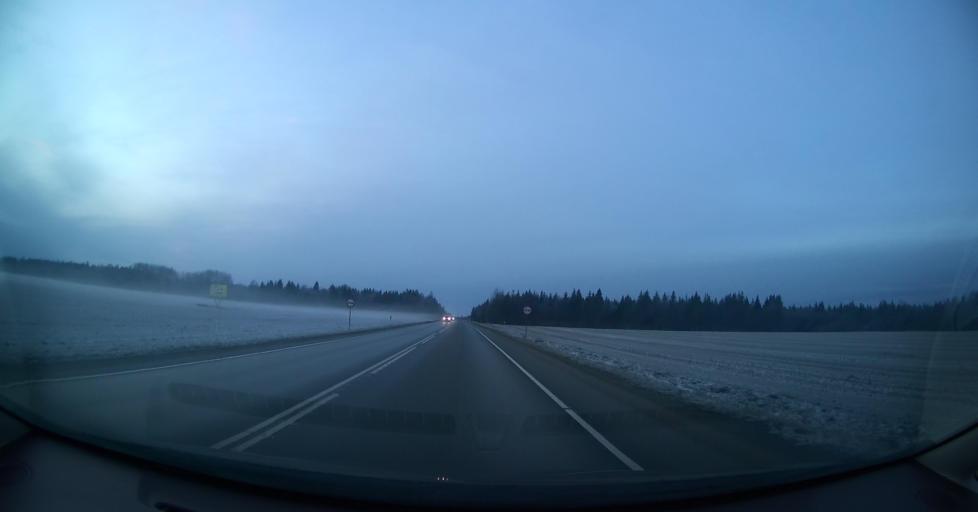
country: EE
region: Jaervamaa
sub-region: Paide linn
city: Paide
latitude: 58.8942
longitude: 25.6667
